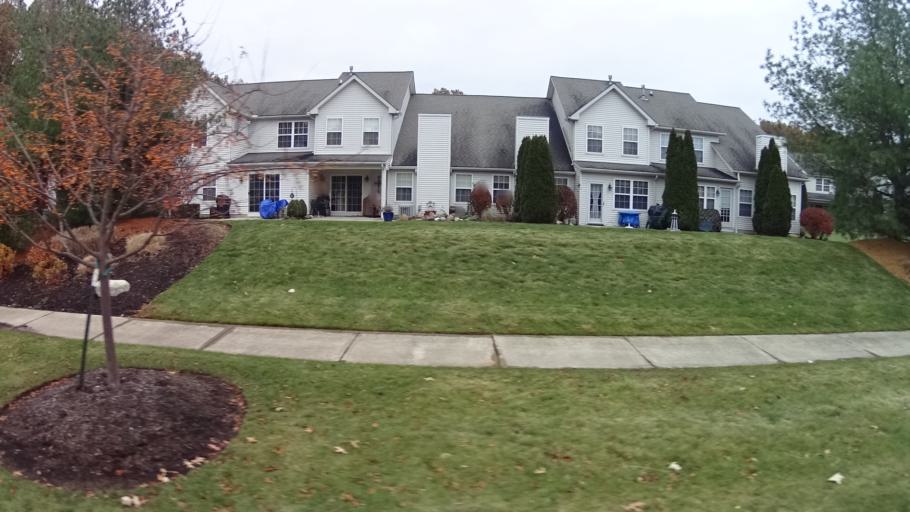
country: US
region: Ohio
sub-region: Lorain County
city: Avon Center
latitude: 41.4812
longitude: -82.0161
